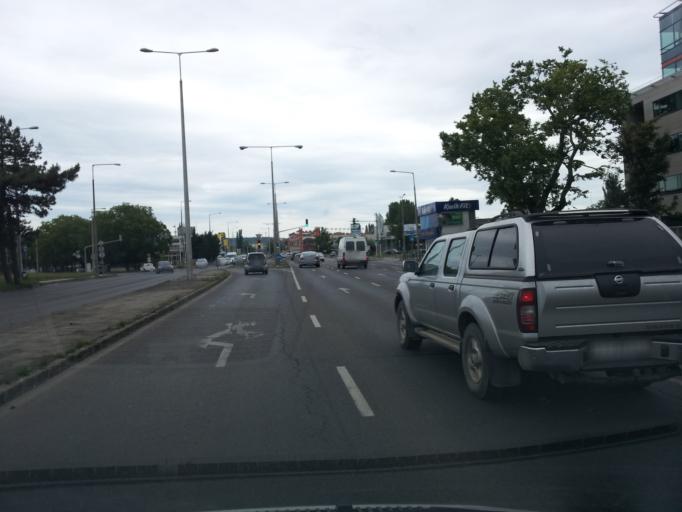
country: HU
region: Budapest
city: Budapest III. keruelet
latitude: 47.5779
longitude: 19.0491
